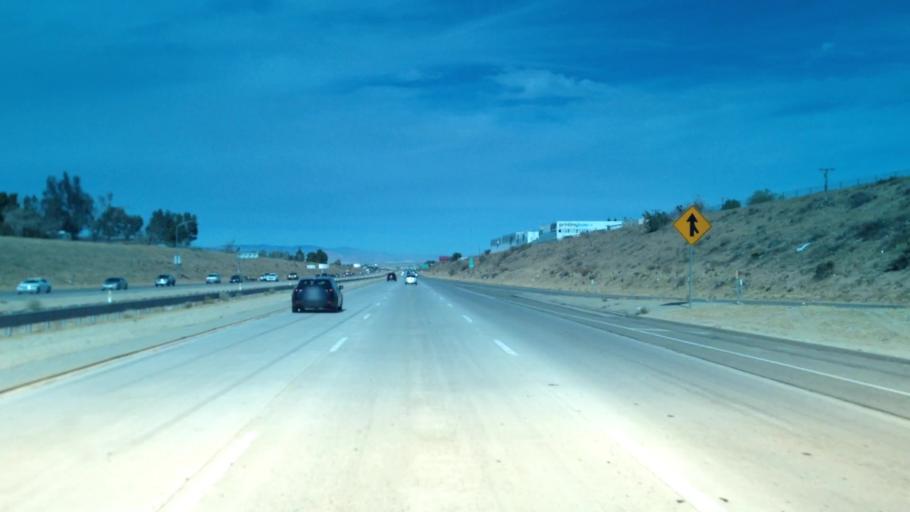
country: US
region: California
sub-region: Los Angeles County
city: Lancaster
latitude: 34.6475
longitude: -118.1526
